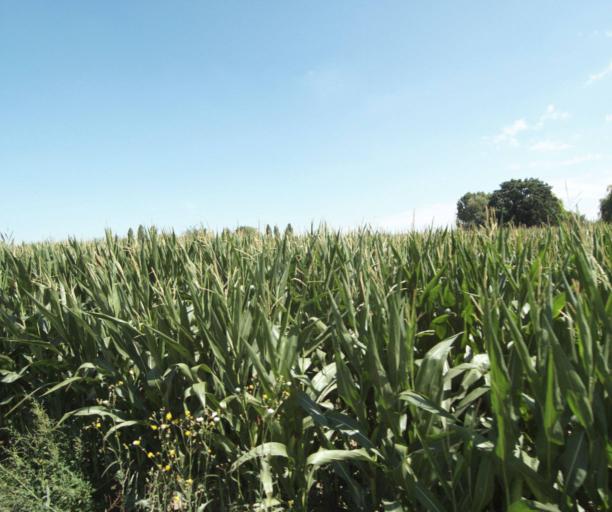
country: FR
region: Nord-Pas-de-Calais
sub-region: Departement du Nord
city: Neuville-en-Ferrain
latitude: 50.7632
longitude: 3.1522
